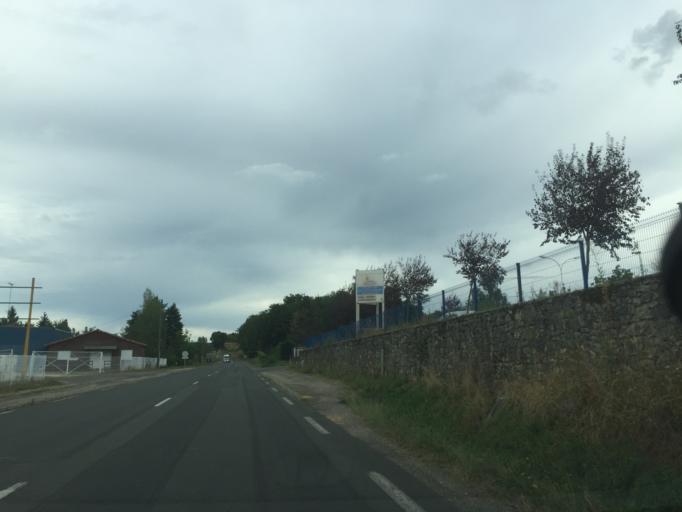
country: FR
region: Aquitaine
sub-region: Departement du Lot-et-Garonne
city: Monsempron-Libos
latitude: 44.4990
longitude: 0.9463
